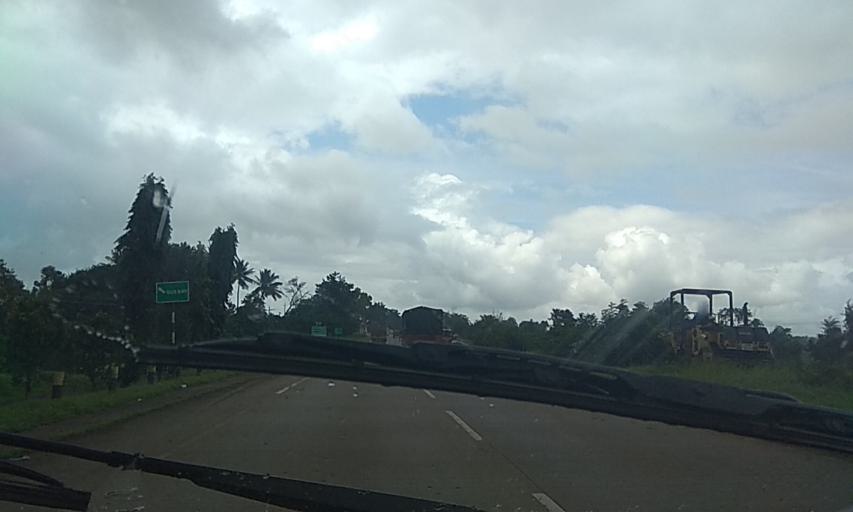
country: IN
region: Karnataka
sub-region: Belgaum
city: Sankeshwar
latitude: 16.2942
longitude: 74.4384
